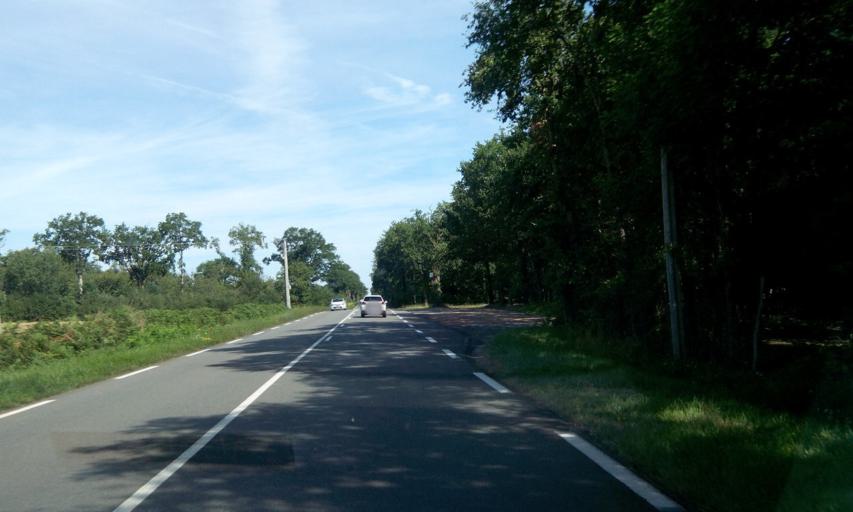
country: FR
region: Poitou-Charentes
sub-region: Departement de la Vienne
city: Availles-Limouzine
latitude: 46.0746
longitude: 0.5920
